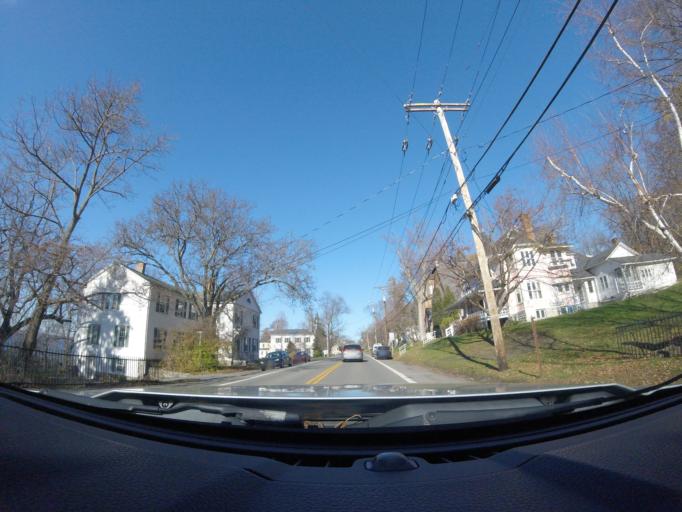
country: US
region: New York
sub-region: Cayuga County
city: Union Springs
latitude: 42.7507
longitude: -76.7013
